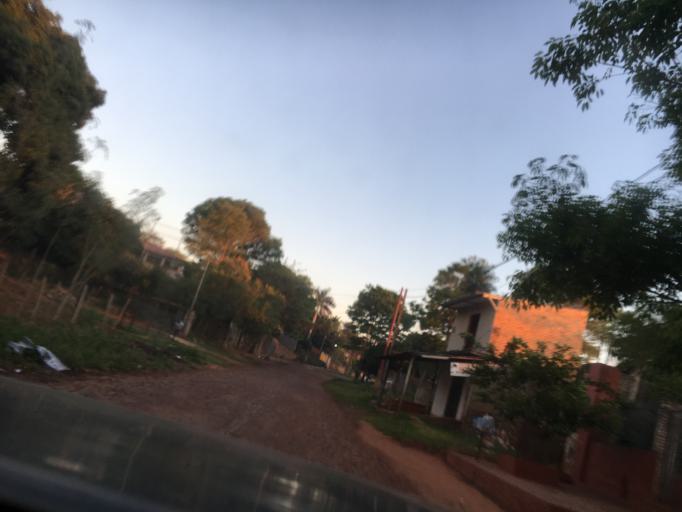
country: PY
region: Central
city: Villa Elisa
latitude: -25.3594
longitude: -57.5914
